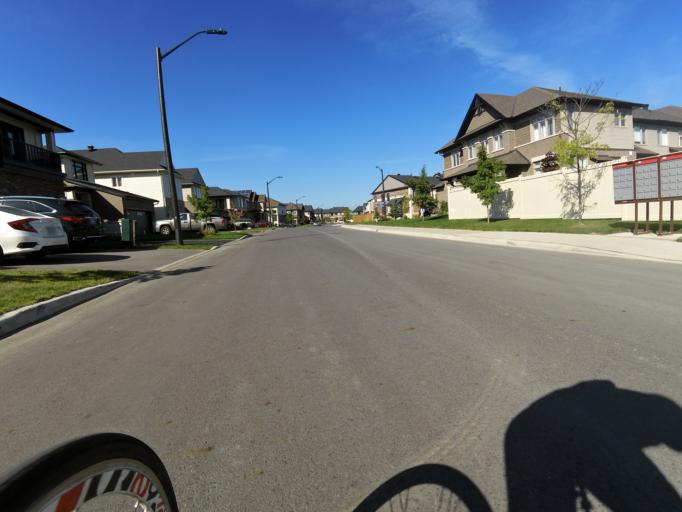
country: CA
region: Ontario
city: Bells Corners
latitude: 45.2661
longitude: -75.6987
